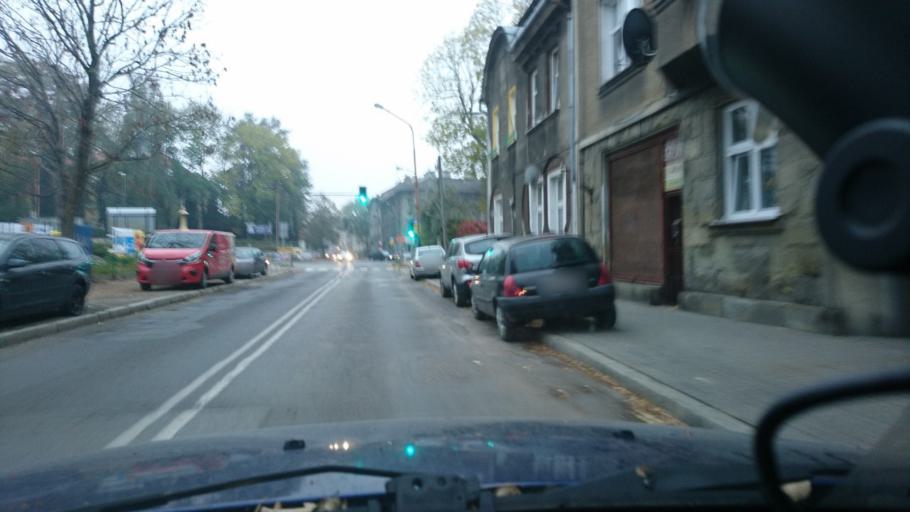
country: PL
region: Silesian Voivodeship
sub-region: Bielsko-Biala
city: Bielsko-Biala
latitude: 49.8257
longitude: 19.0579
